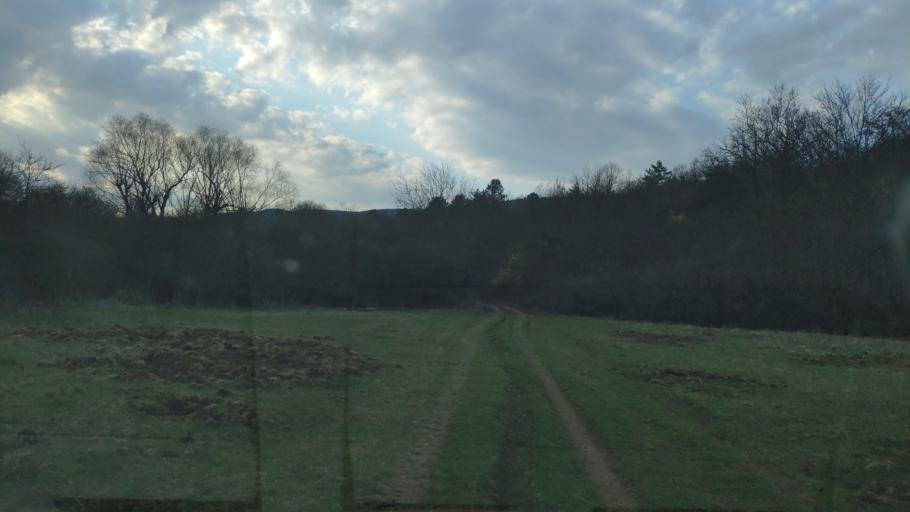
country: SK
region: Kosicky
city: Moldava nad Bodvou
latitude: 48.6164
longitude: 20.9162
